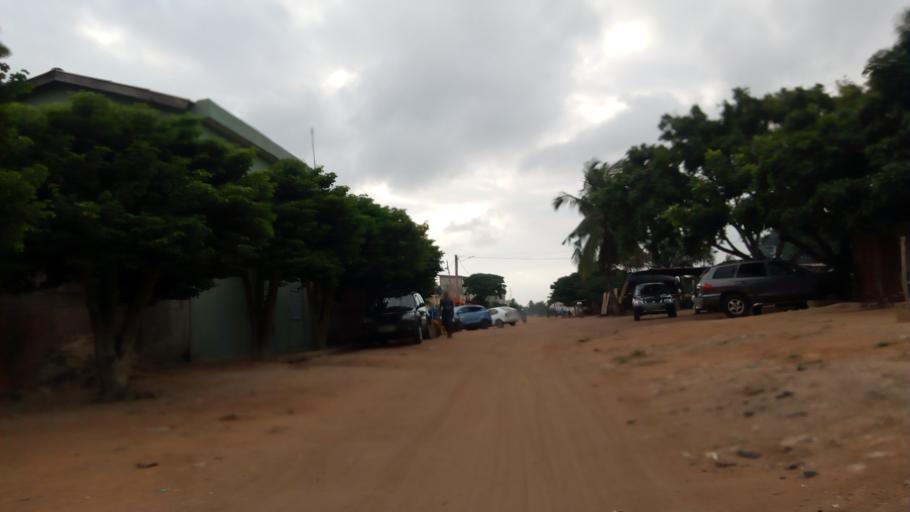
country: TG
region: Maritime
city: Lome
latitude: 6.1794
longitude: 1.1865
